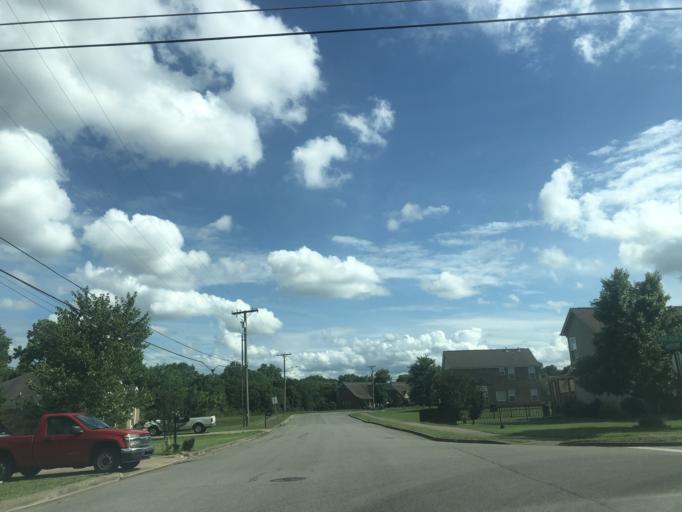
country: US
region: Tennessee
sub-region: Davidson County
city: Nashville
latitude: 36.2211
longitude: -86.8667
